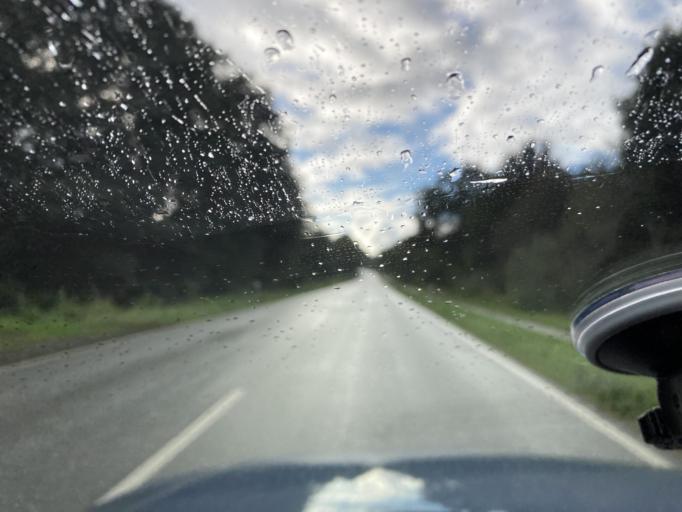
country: DE
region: Schleswig-Holstein
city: Tellingstedt
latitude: 54.2196
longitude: 9.3124
